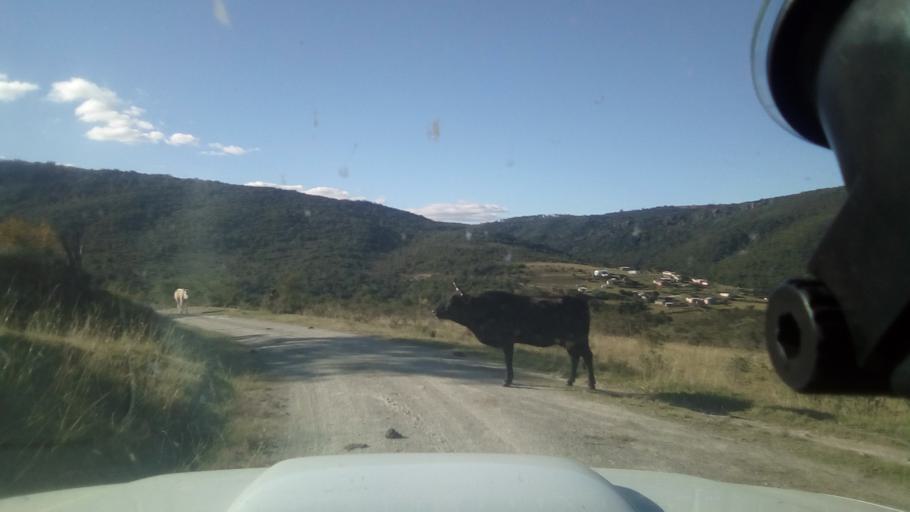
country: ZA
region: Eastern Cape
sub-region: Buffalo City Metropolitan Municipality
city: Bhisho
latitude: -32.7311
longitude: 27.3481
